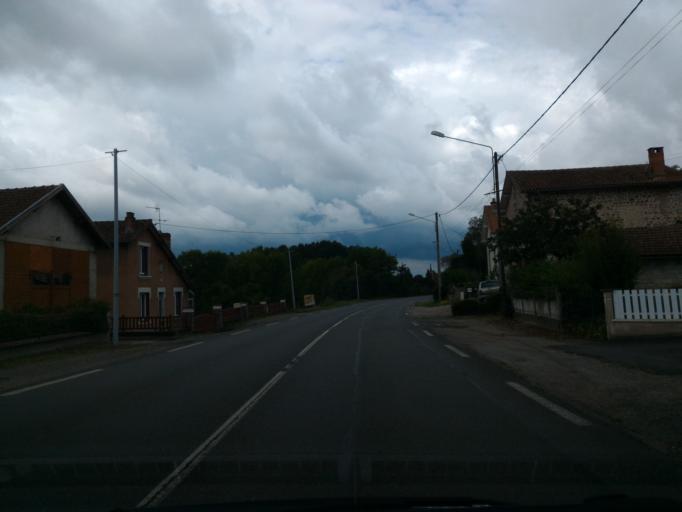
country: FR
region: Poitou-Charentes
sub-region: Departement de la Charente
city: Chabanais
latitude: 45.8785
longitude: 0.7312
